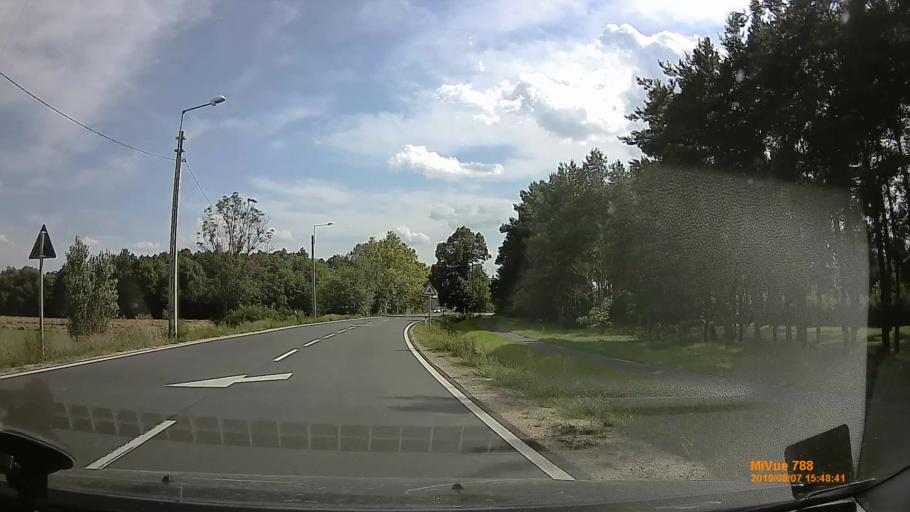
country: HU
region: Vas
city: Jak
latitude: 47.1590
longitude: 16.6384
